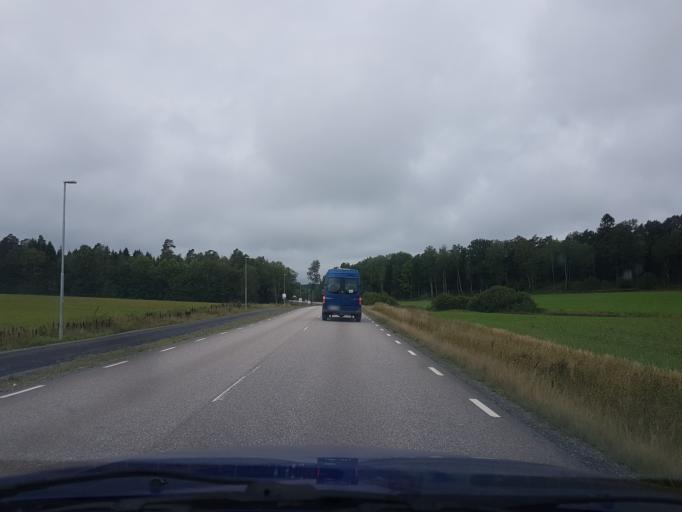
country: SE
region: Vaestra Goetaland
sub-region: Ale Kommun
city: Alvangen
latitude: 57.9389
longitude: 12.1541
